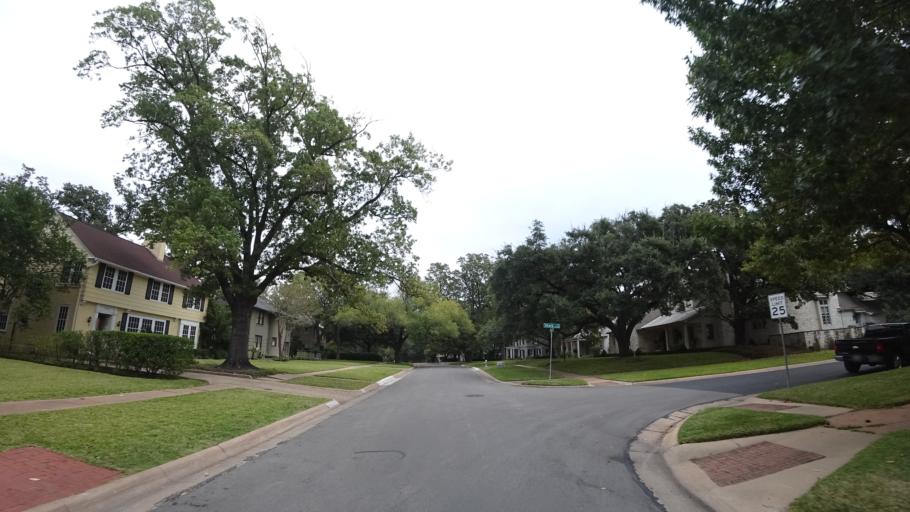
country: US
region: Texas
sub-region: Travis County
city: Austin
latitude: 30.2929
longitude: -97.7547
